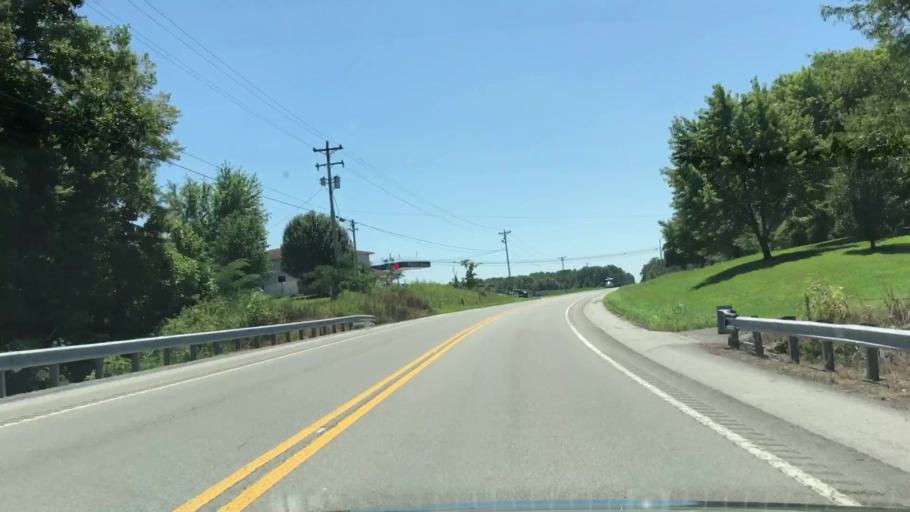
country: US
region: Tennessee
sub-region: Jackson County
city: Dodson Branch
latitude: 36.2606
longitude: -85.6107
